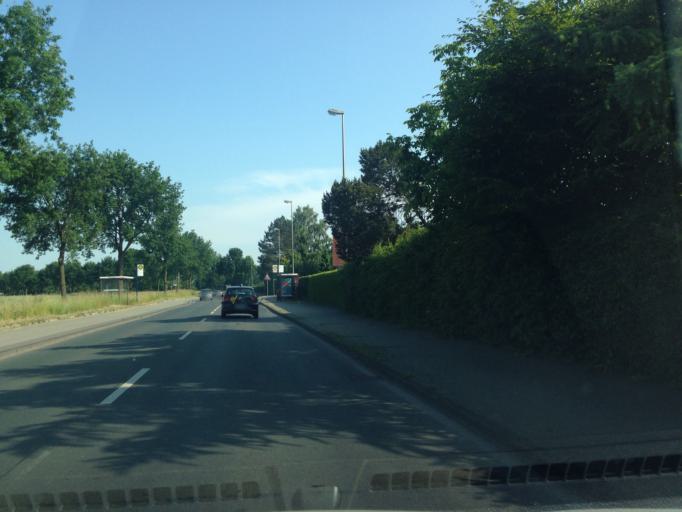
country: DE
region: North Rhine-Westphalia
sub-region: Regierungsbezirk Munster
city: Muenster
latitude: 51.9380
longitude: 7.5737
